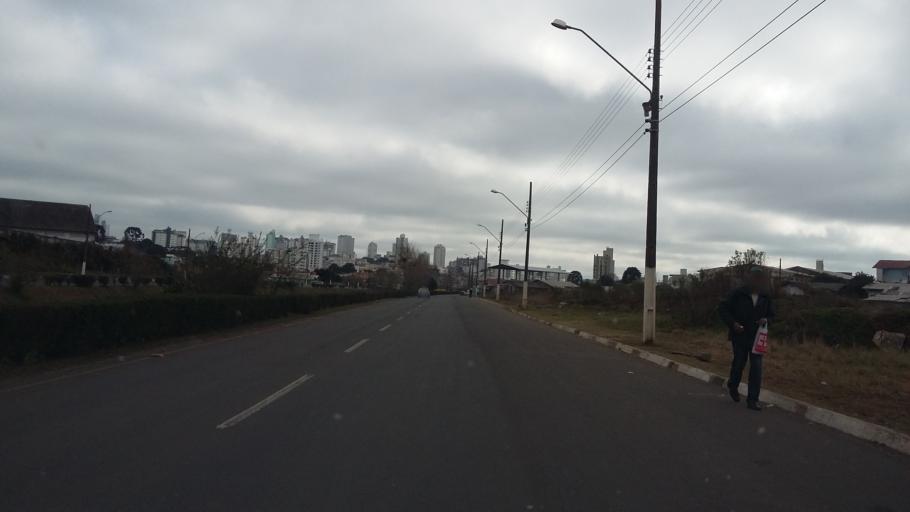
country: BR
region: Santa Catarina
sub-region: Lages
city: Lages
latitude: -27.8302
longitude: -50.3205
